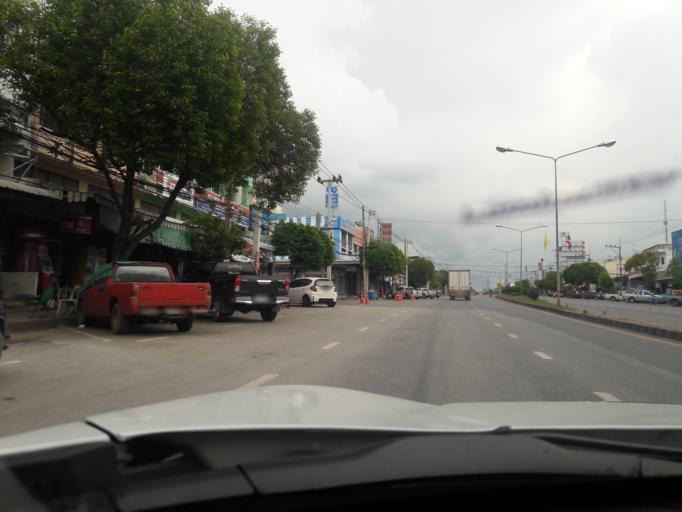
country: TH
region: Lop Buri
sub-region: Amphoe Tha Luang
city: Tha Luang
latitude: 15.0712
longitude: 101.1095
